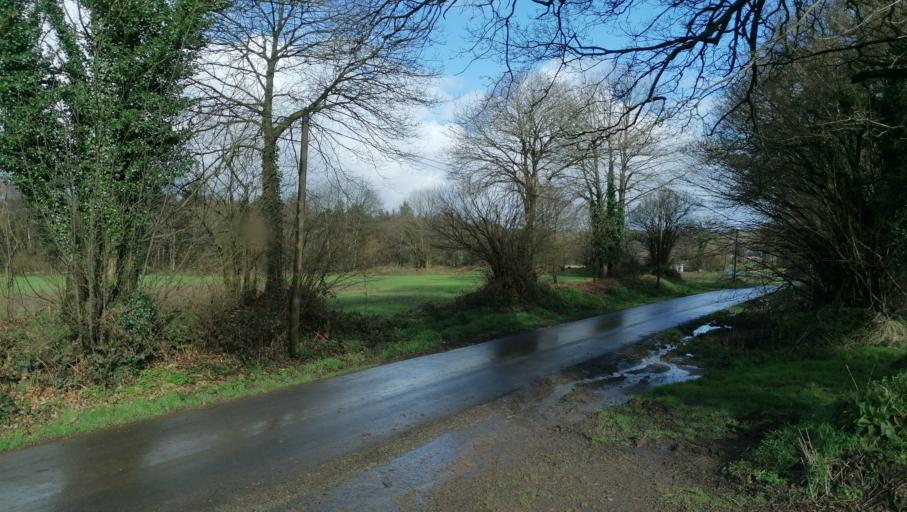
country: FR
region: Brittany
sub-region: Departement des Cotes-d'Armor
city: Lanrodec
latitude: 48.4885
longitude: -3.0267
